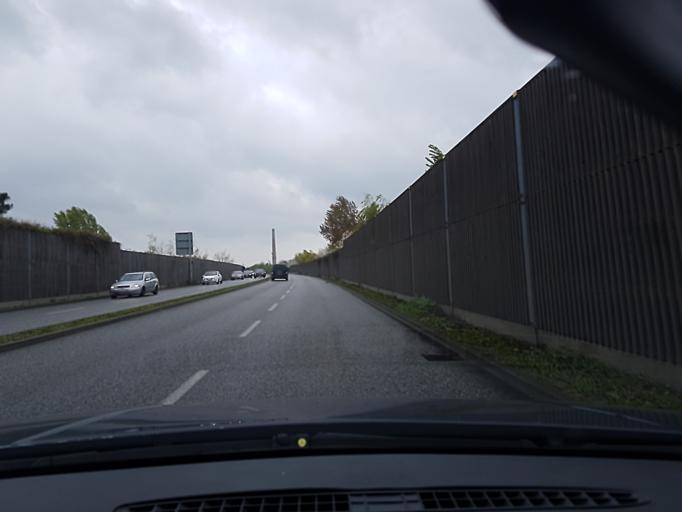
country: DE
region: Berlin
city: Adlershof
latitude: 52.4437
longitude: 13.5591
